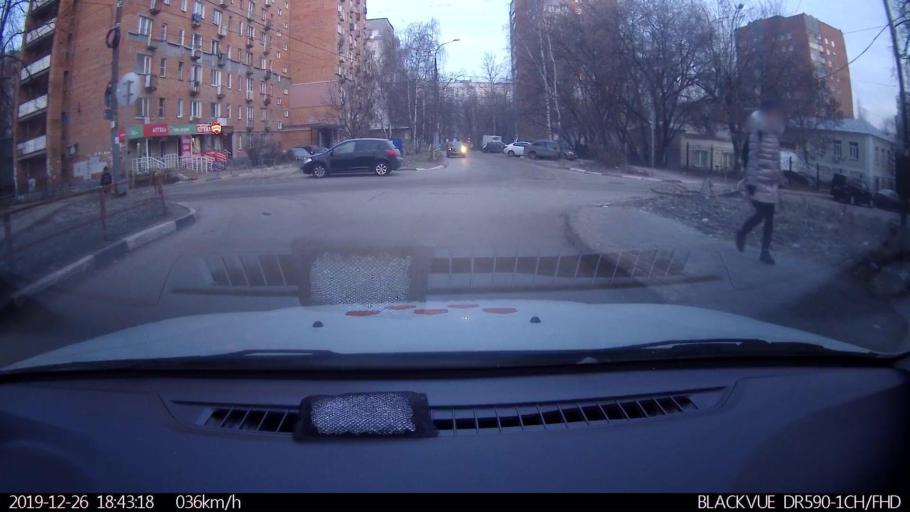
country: RU
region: Nizjnij Novgorod
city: Nizhniy Novgorod
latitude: 56.3182
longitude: 44.0298
